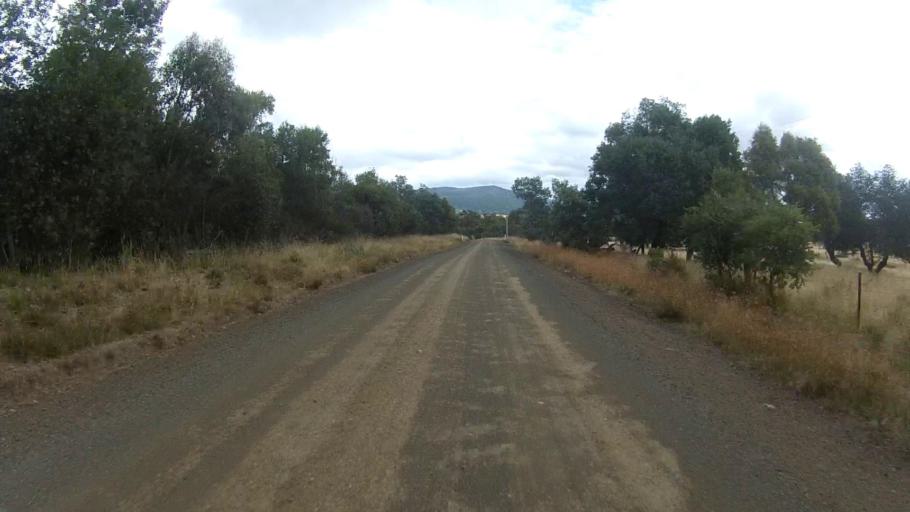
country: AU
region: Tasmania
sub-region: Break O'Day
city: St Helens
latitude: -41.8219
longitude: 147.9889
